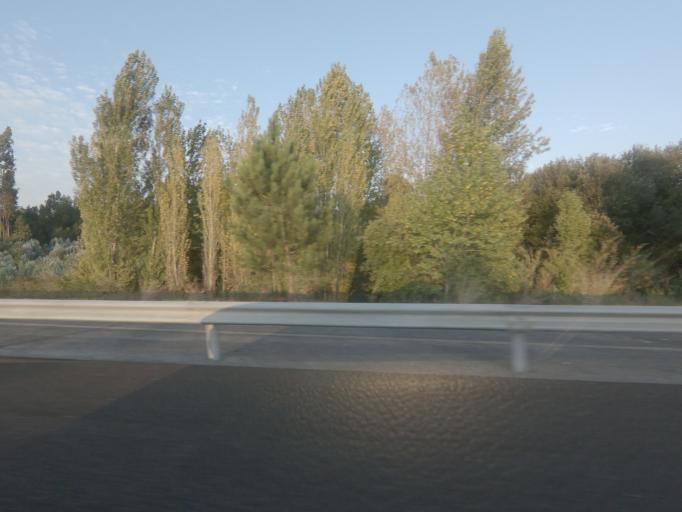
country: PT
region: Leiria
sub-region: Leiria
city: Caranguejeira
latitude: 39.7692
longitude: -8.7443
